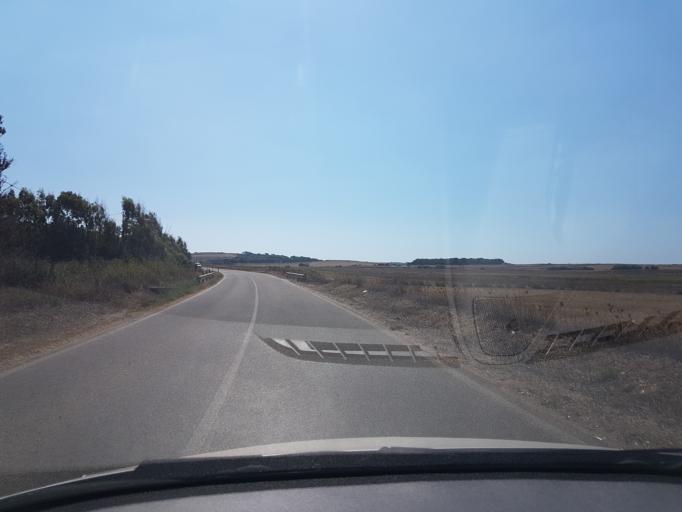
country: IT
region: Sardinia
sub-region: Provincia di Oristano
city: Nurachi
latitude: 39.9906
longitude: 8.4615
